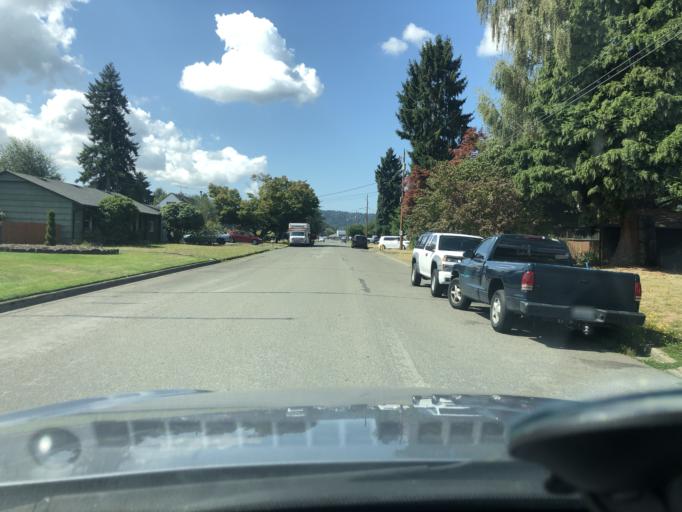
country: US
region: Washington
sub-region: King County
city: Auburn
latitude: 47.3223
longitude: -122.2158
